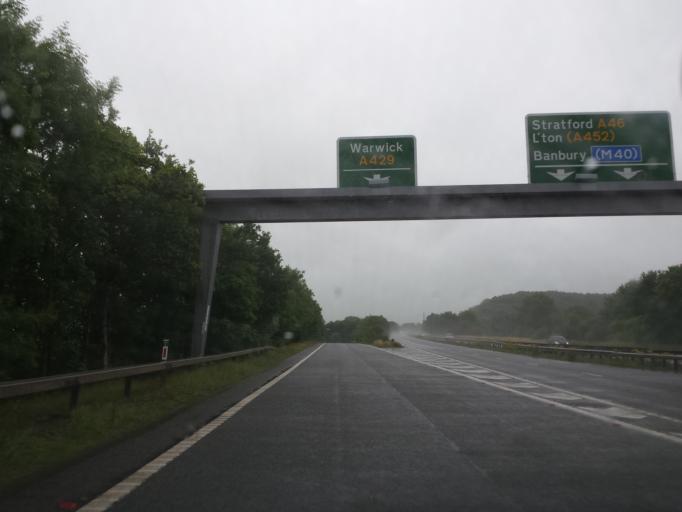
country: GB
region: England
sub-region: Warwickshire
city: Warwick
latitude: 52.3111
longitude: -1.5715
